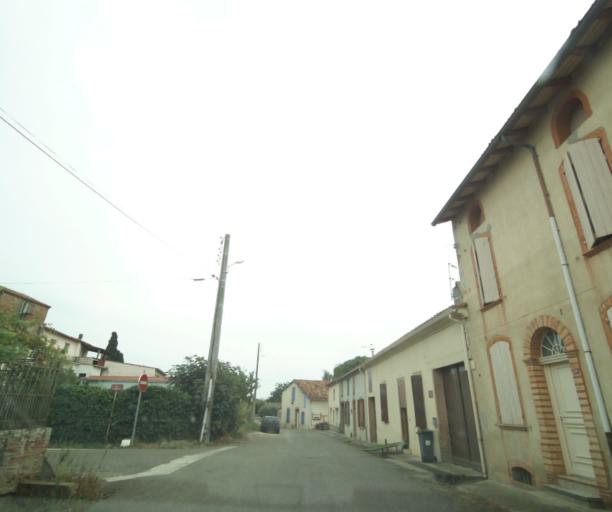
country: FR
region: Midi-Pyrenees
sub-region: Departement du Tarn-et-Garonne
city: Saint-Porquier
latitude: 43.9840
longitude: 1.1878
